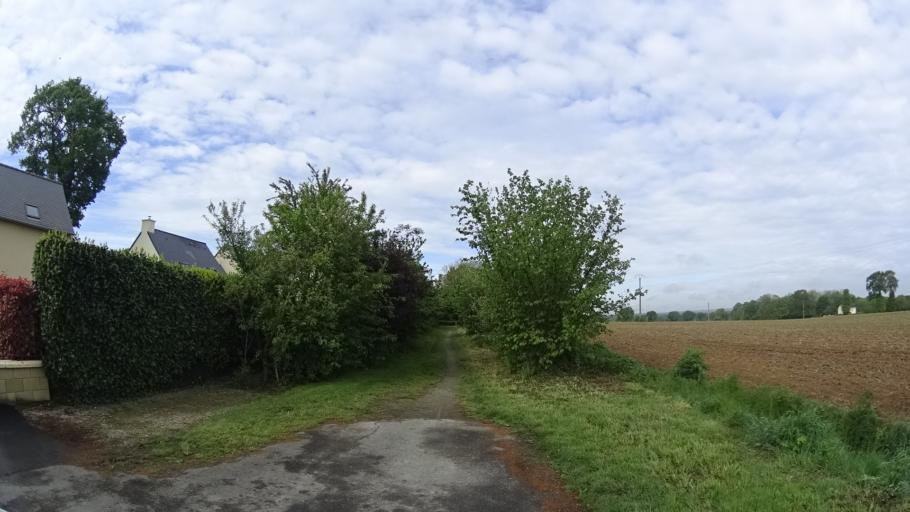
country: FR
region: Brittany
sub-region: Departement d'Ille-et-Vilaine
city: Mordelles
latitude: 48.0818
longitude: -1.8400
